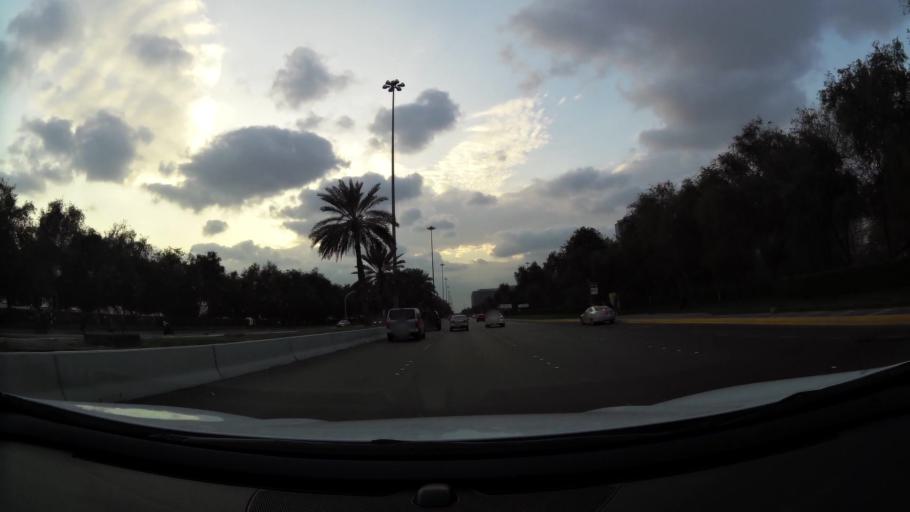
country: AE
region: Abu Dhabi
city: Abu Dhabi
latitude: 24.4270
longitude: 54.4400
